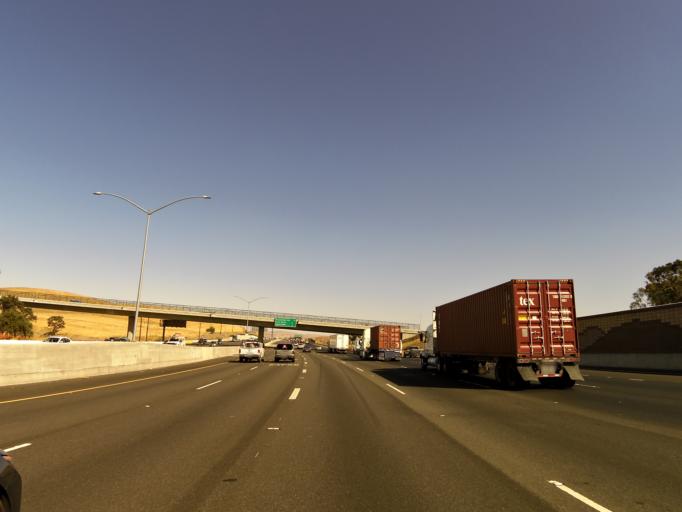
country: US
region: California
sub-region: Alameda County
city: Livermore
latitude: 37.6990
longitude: -121.7881
